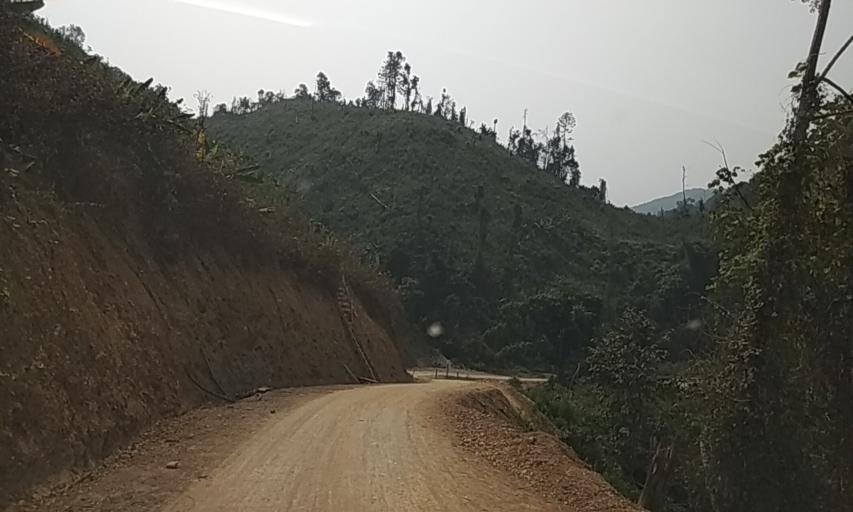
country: LA
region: Phongsali
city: Phongsali
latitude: 21.4693
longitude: 102.4323
